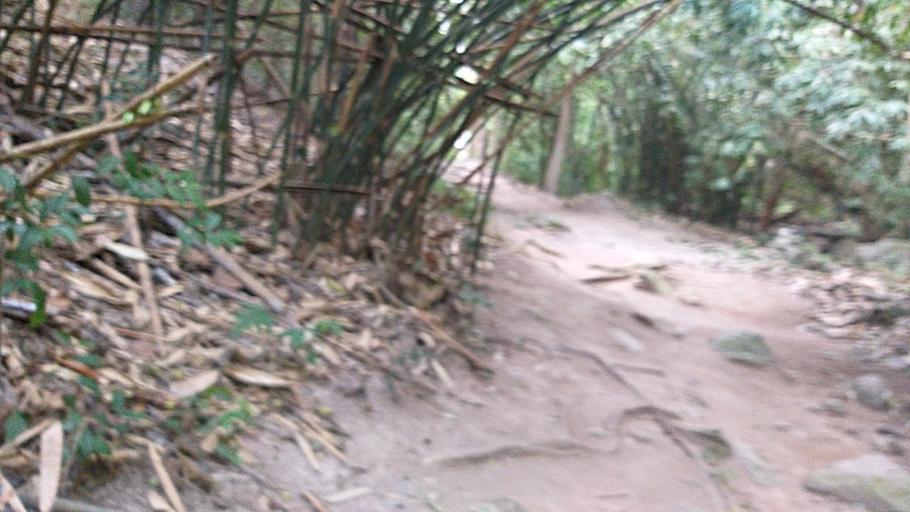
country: TH
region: Sara Buri
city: Wihan Daeng
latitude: 14.4358
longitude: 100.9628
